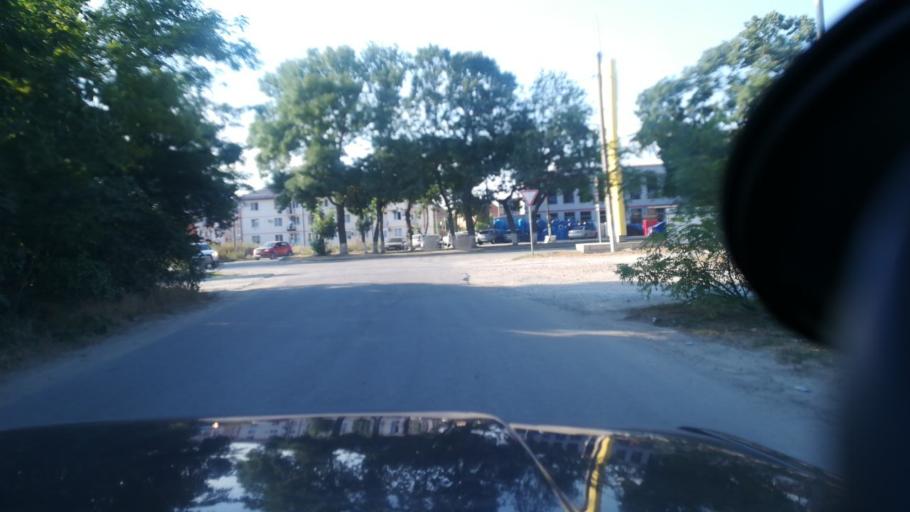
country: RU
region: Krasnodarskiy
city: Vityazevo
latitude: 45.0015
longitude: 37.2923
